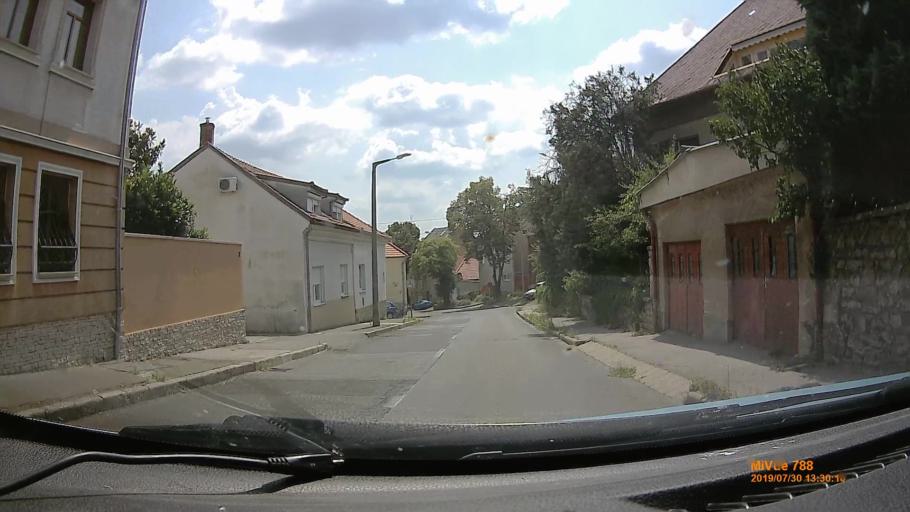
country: HU
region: Baranya
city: Pecs
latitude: 46.0810
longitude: 18.2203
